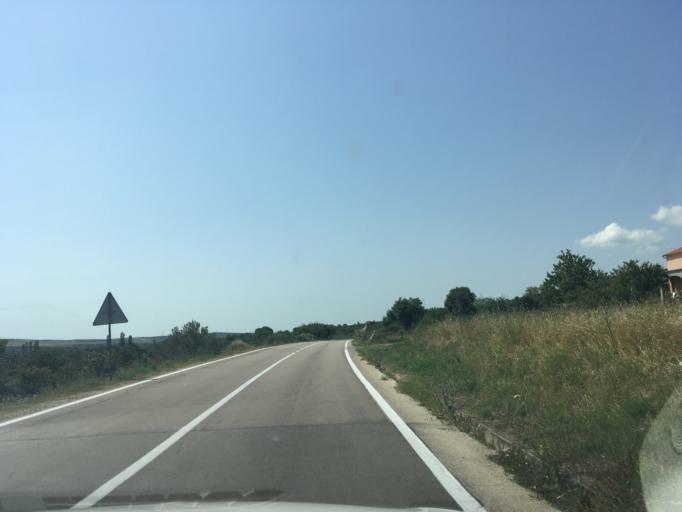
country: HR
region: Zadarska
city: Benkovac
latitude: 43.9679
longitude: 15.7207
